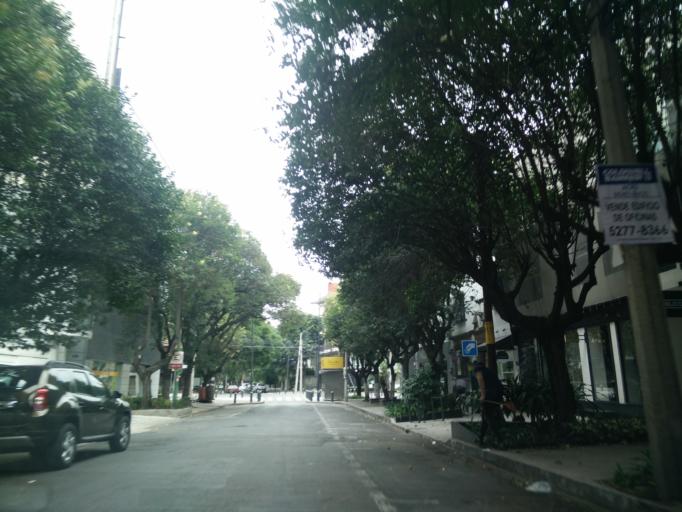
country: MX
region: Mexico City
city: Miguel Hidalgo
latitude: 19.4316
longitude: -99.2028
